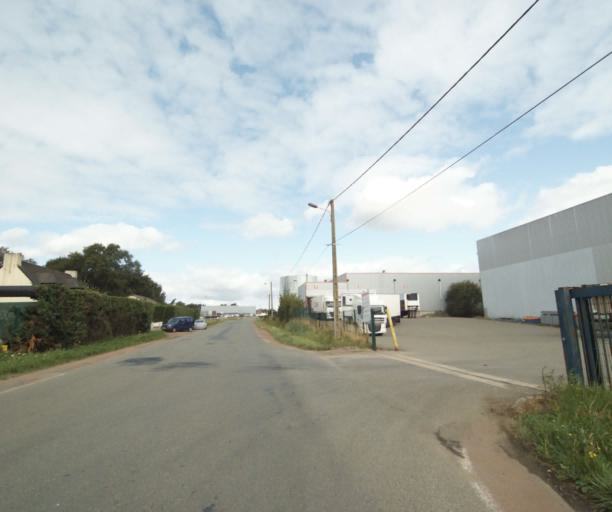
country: FR
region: Pays de la Loire
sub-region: Departement de la Sarthe
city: Sable-sur-Sarthe
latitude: 47.8252
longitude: -0.3103
